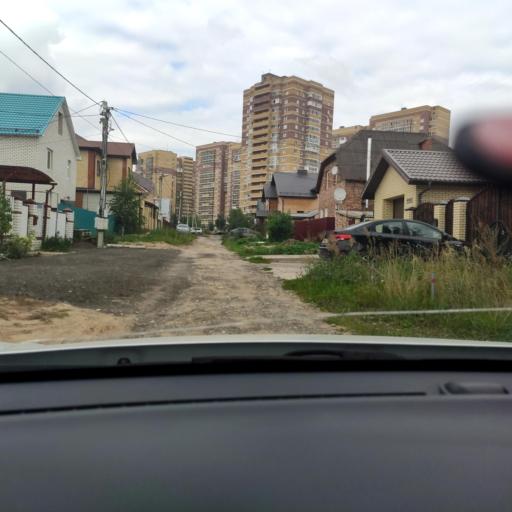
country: RU
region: Tatarstan
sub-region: Gorod Kazan'
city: Kazan
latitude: 55.7784
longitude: 49.2429
